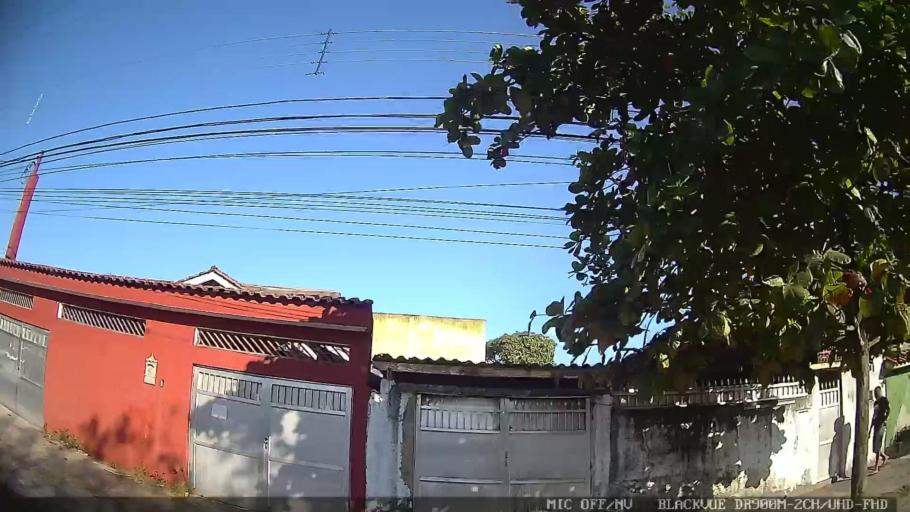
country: BR
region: Sao Paulo
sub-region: Guaruja
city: Guaruja
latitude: -23.9632
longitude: -46.2804
